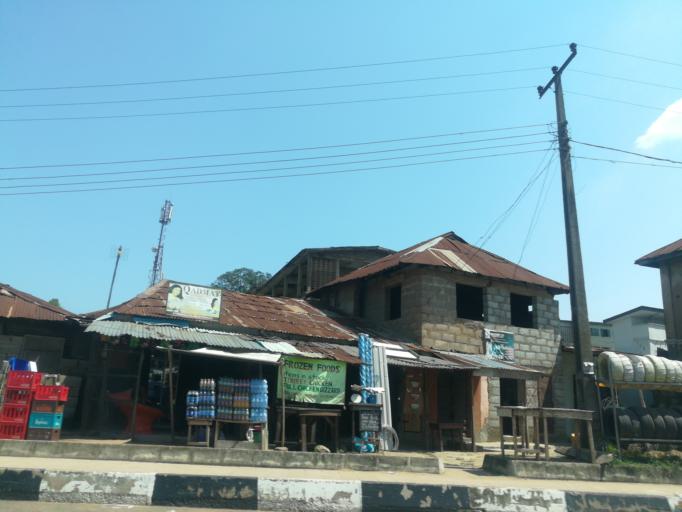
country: NG
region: Ogun
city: Abeokuta
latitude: 7.1625
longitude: 3.3506
